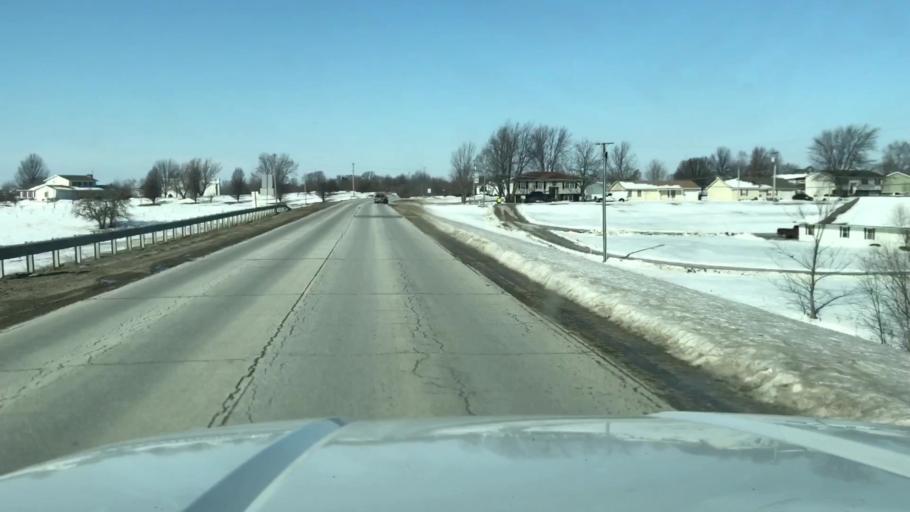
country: US
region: Missouri
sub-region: Andrew County
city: Savannah
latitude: 39.9492
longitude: -94.8431
